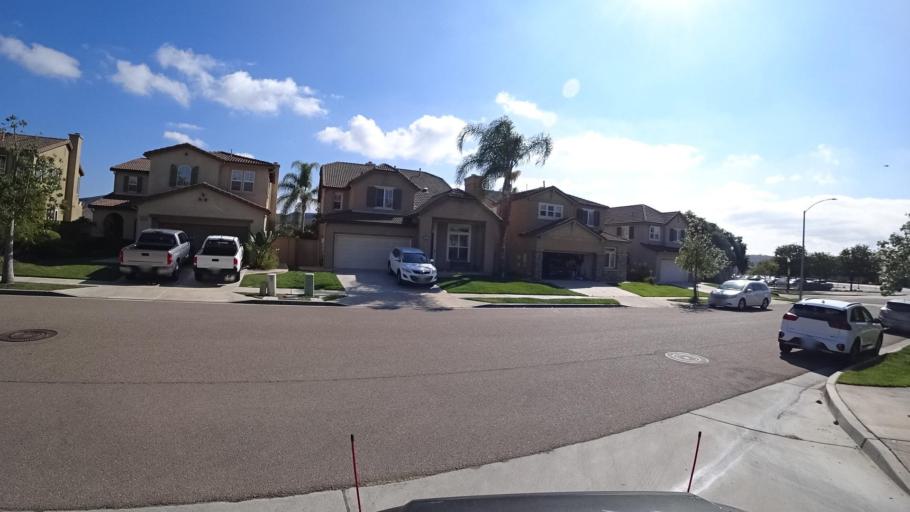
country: US
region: California
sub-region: San Diego County
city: Fairbanks Ranch
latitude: 33.0057
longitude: -117.1152
